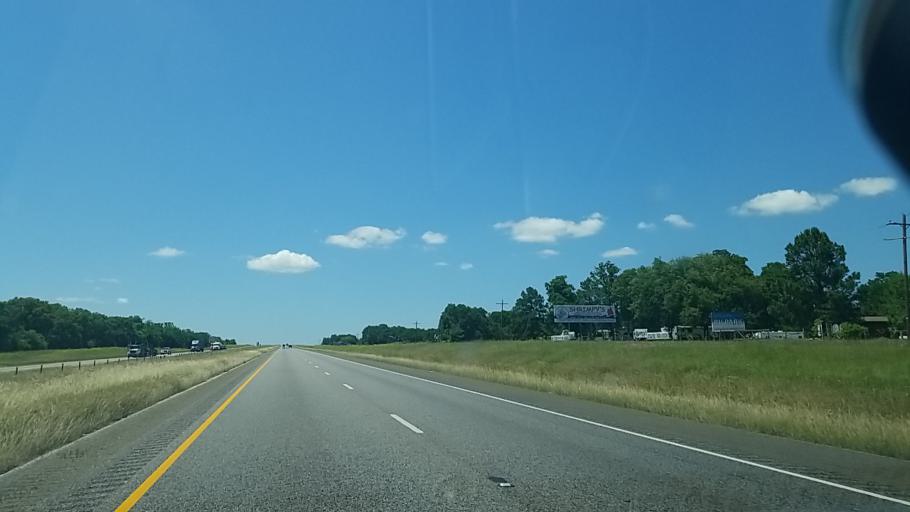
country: US
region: Texas
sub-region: Madison County
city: Madisonville
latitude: 30.9407
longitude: -95.8443
